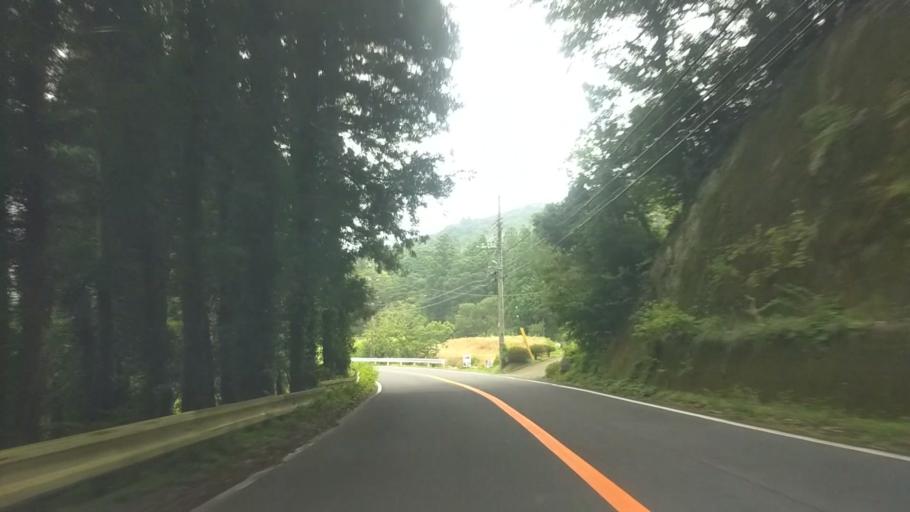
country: JP
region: Chiba
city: Kawaguchi
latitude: 35.2165
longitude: 140.0718
